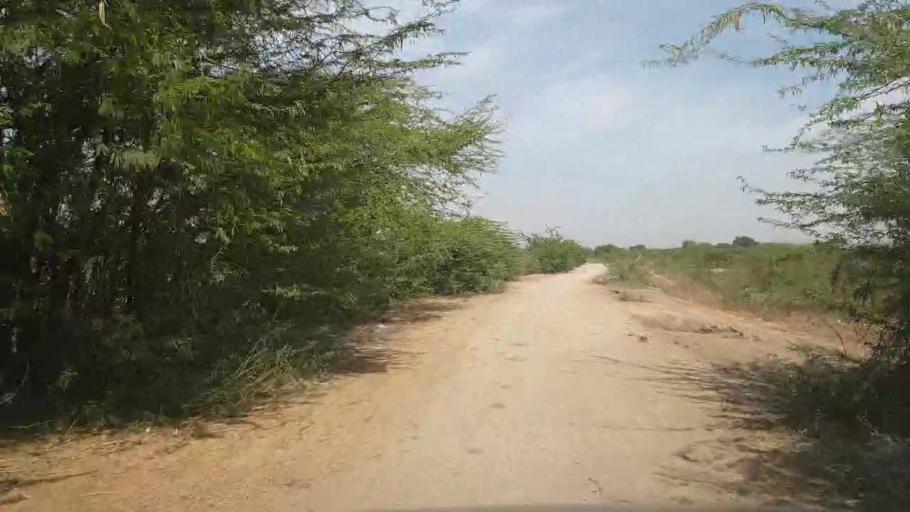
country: PK
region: Sindh
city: Kunri
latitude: 25.2414
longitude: 69.6766
